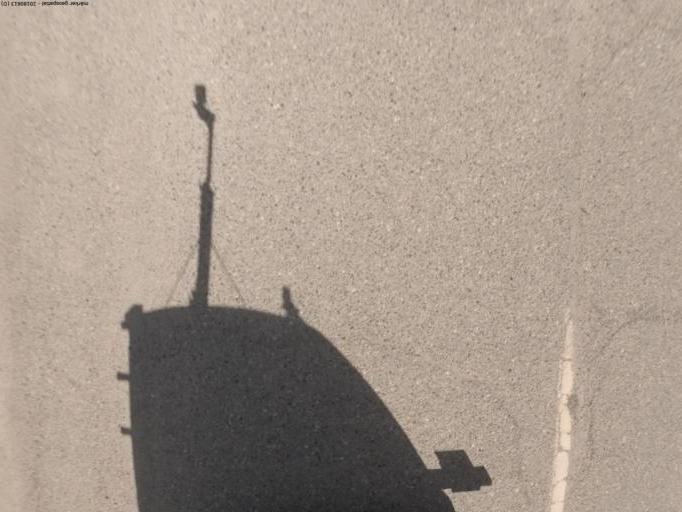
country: US
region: California
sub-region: Madera County
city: Fairmead
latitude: 37.0847
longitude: -120.2264
